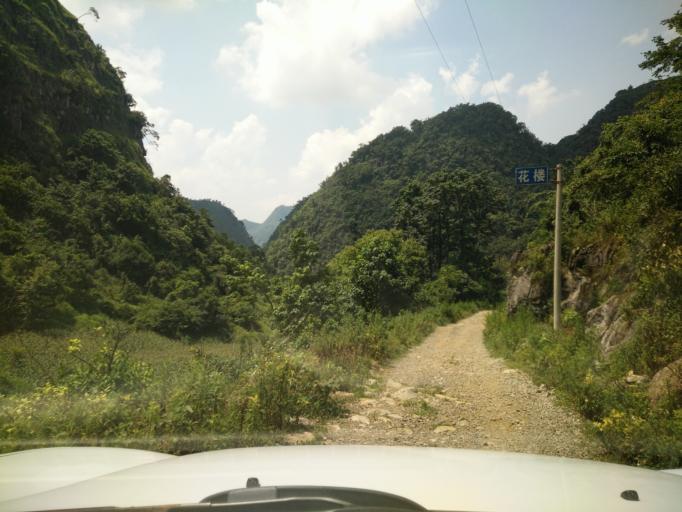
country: CN
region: Guangxi Zhuangzu Zizhiqu
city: Xinzhou
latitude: 25.0167
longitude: 105.7049
